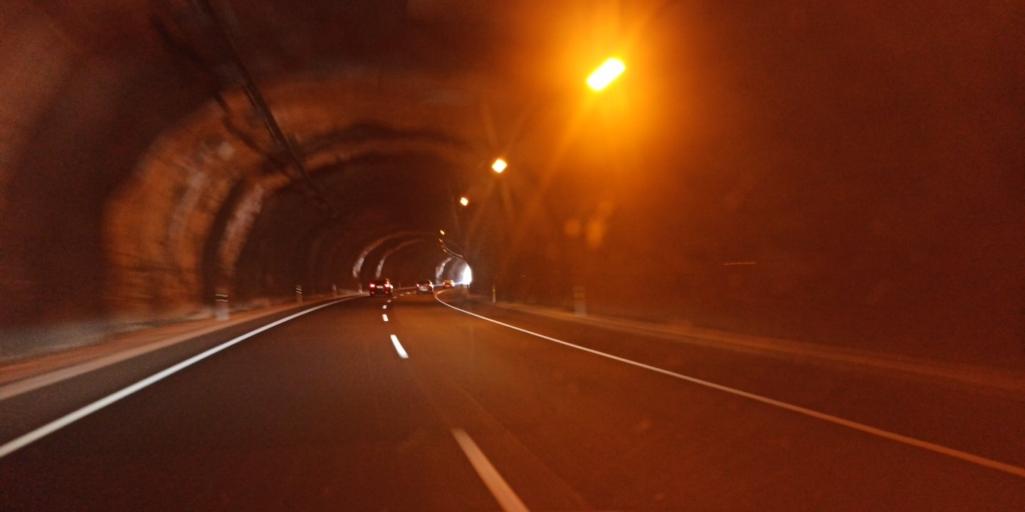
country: ES
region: Catalonia
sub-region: Provincia de Barcelona
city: Sant Pere de Ribes
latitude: 41.3006
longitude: 1.7262
